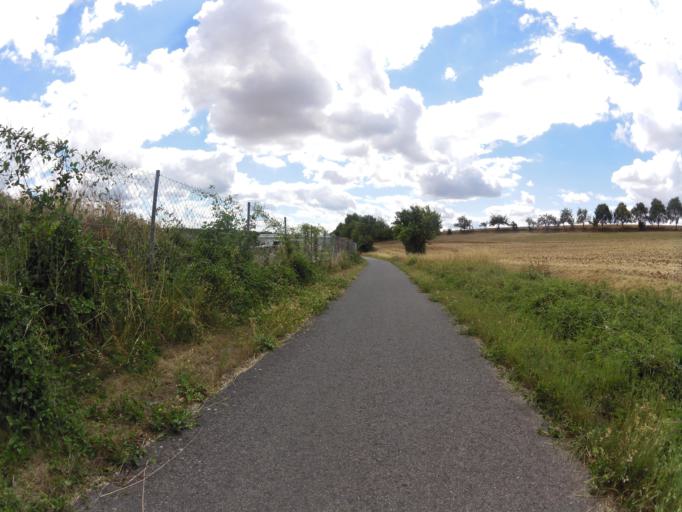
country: DE
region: Bavaria
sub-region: Regierungsbezirk Unterfranken
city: Aub
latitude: 49.5545
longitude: 10.0535
